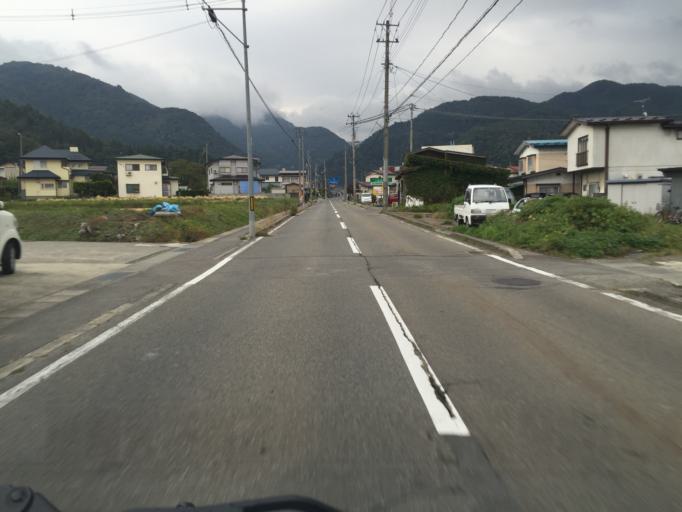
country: JP
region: Fukushima
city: Kitakata
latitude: 37.4902
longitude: 139.9479
